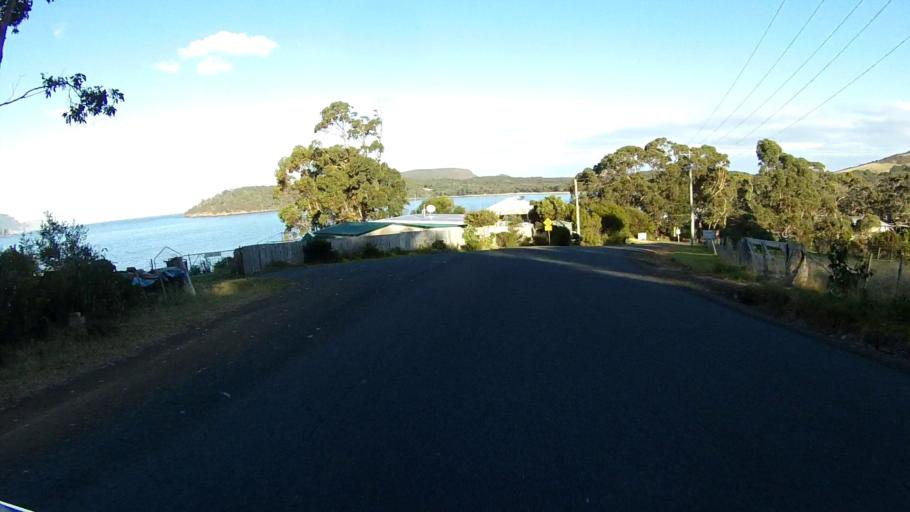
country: AU
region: Tasmania
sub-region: Clarence
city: Sandford
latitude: -43.1736
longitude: 147.8548
